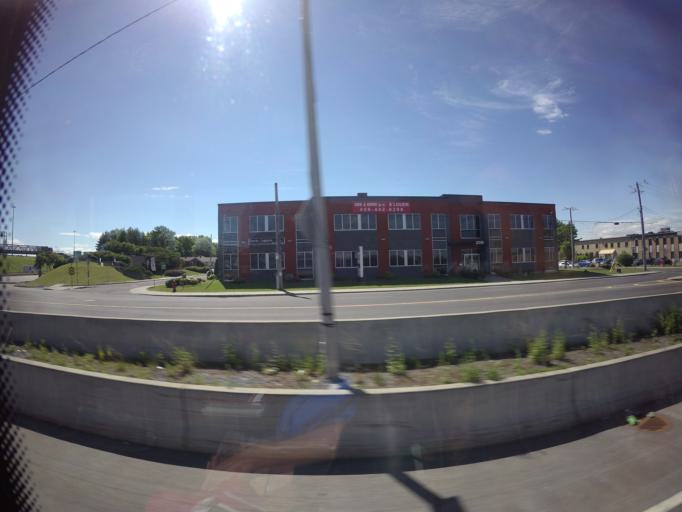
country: CA
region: Quebec
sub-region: Monteregie
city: Boucherville
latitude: 45.5778
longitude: -73.4765
